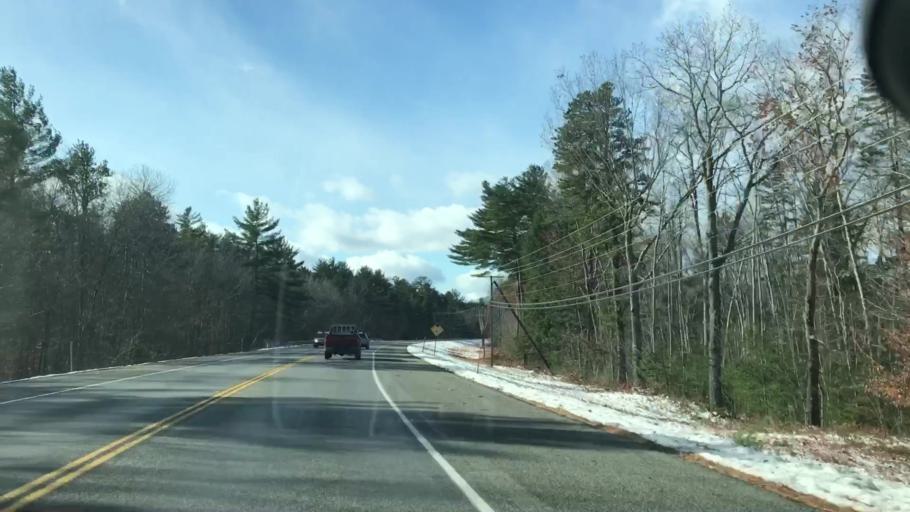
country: US
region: New Hampshire
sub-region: Carroll County
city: Ossipee
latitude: 43.7651
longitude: -71.1247
